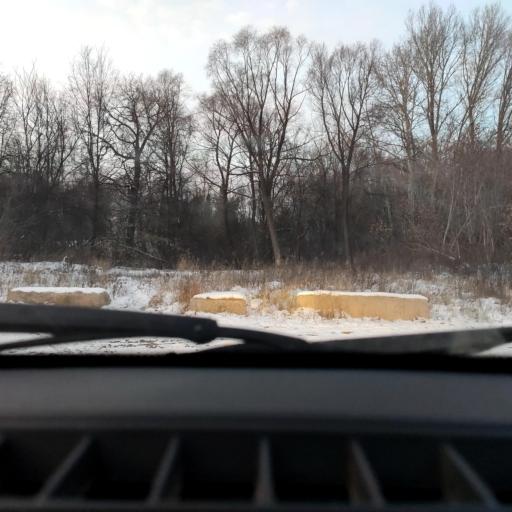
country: RU
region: Bashkortostan
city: Ufa
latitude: 54.7882
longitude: 56.0546
